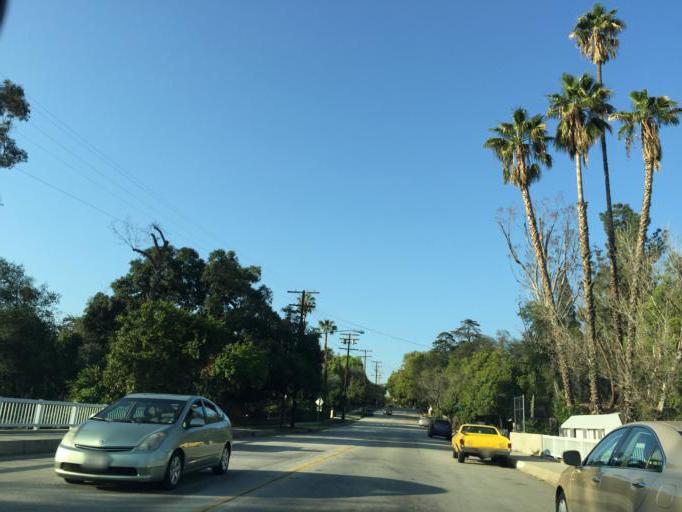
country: US
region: California
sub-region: Los Angeles County
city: South Pasadena
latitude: 34.1189
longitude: -118.1570
